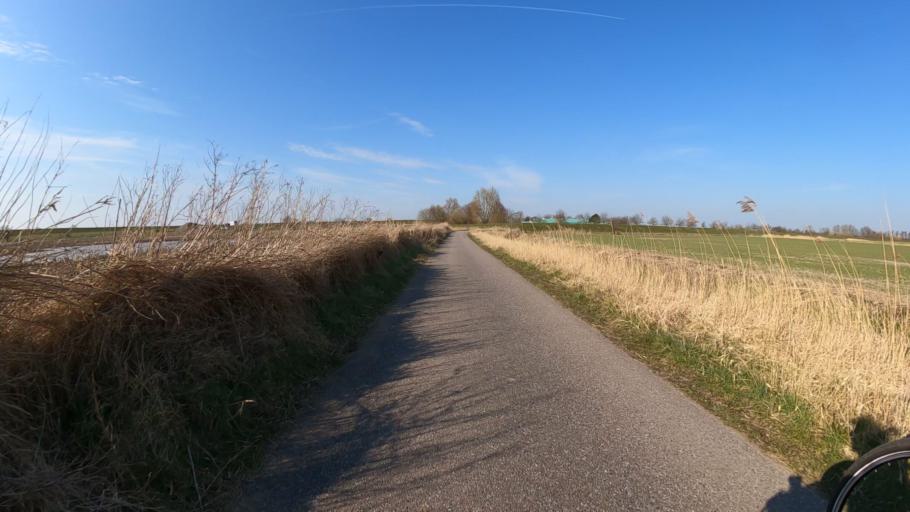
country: DE
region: Schleswig-Holstein
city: Seestermuhe
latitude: 53.7129
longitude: 9.5292
